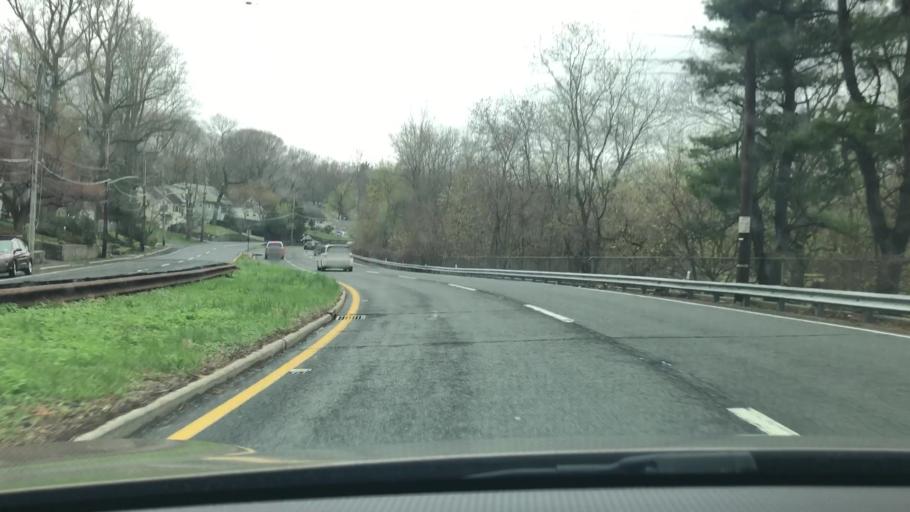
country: US
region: New York
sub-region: Westchester County
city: Mamaroneck
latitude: 40.9680
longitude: -73.7381
